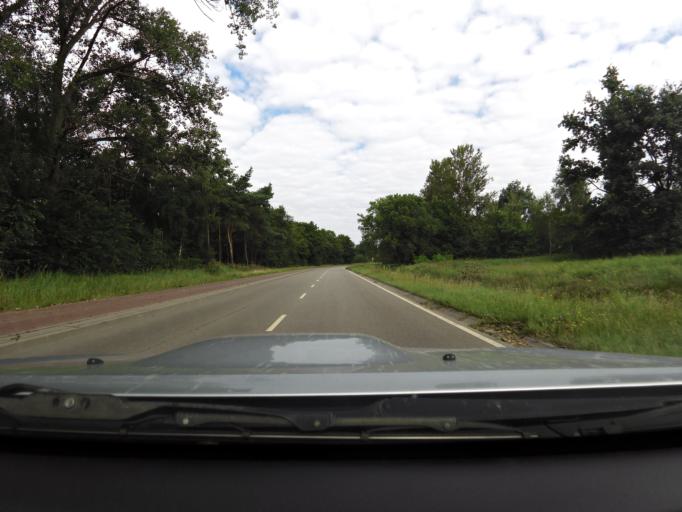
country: PL
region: Pomeranian Voivodeship
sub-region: Gdansk
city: Gdansk
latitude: 54.3994
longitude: 18.6858
